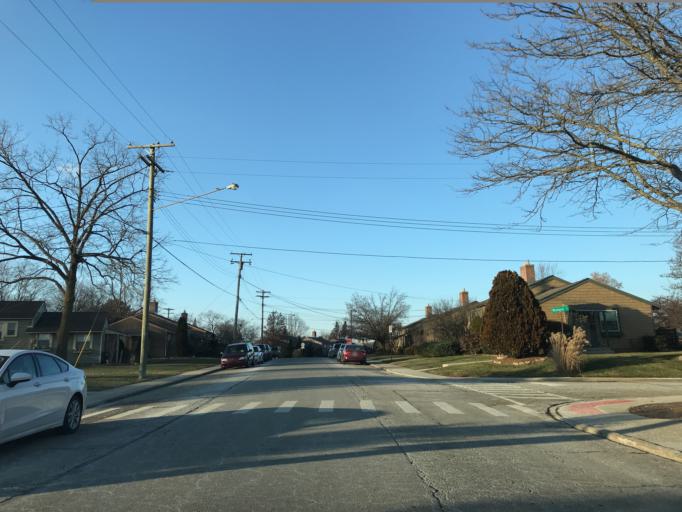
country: US
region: Michigan
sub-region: Washtenaw County
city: Ann Arbor
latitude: 42.2503
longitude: -83.6926
